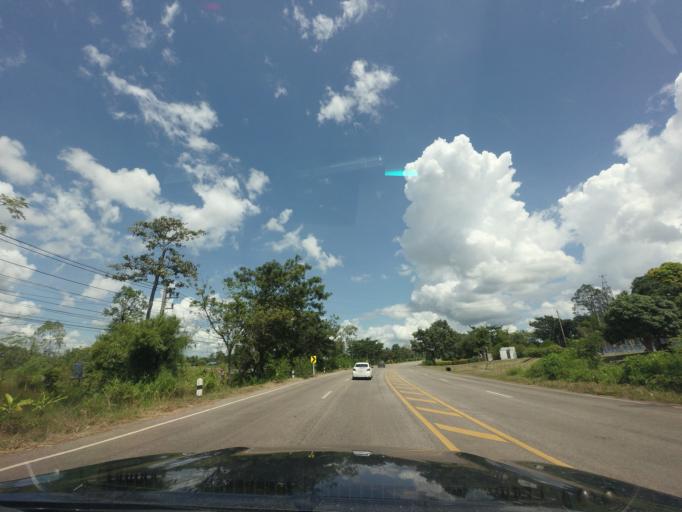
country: TH
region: Changwat Udon Thani
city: Ban Dung
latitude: 17.6860
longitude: 103.1978
